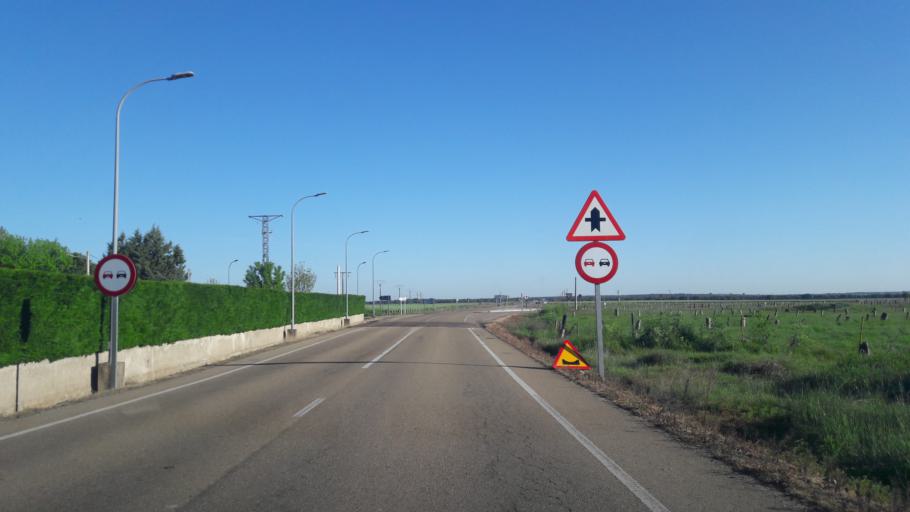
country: ES
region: Castille and Leon
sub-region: Provincia de Salamanca
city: La Fuente de San Esteban
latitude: 40.8043
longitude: -6.2564
